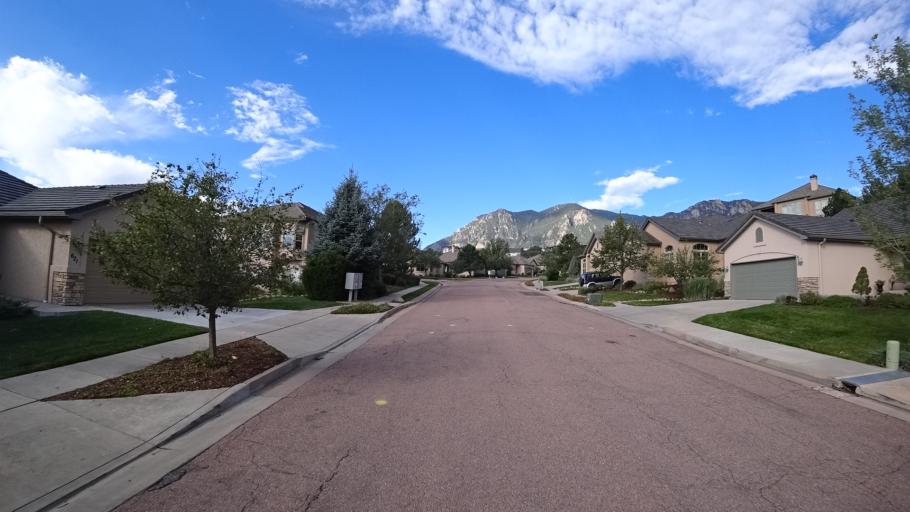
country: US
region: Colorado
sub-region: El Paso County
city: Stratmoor
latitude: 38.7654
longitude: -104.8193
